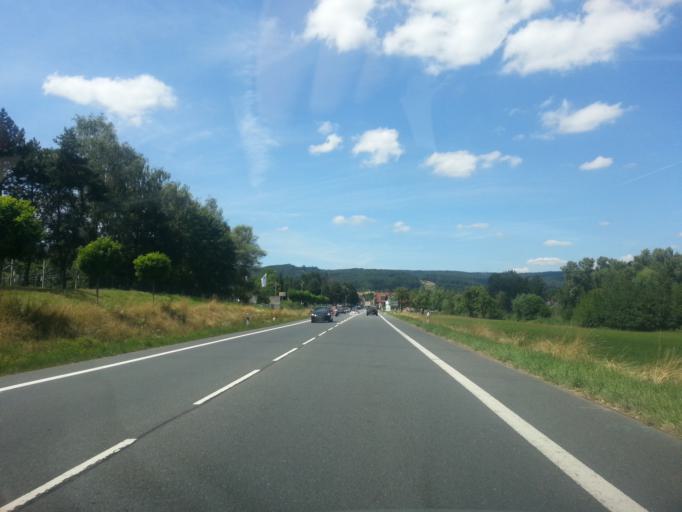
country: DE
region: Hesse
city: Reichelsheim
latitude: 49.7084
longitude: 8.8514
